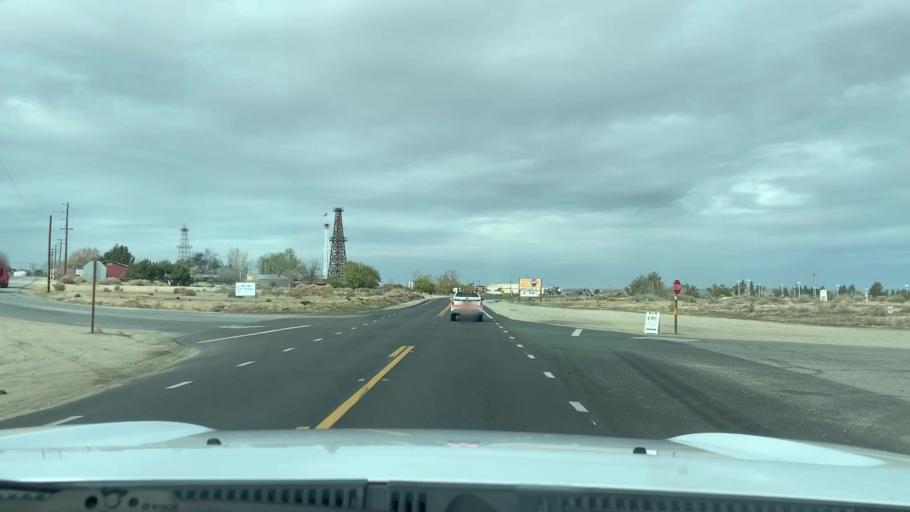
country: US
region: California
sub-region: Kern County
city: South Taft
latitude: 35.1315
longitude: -119.4454
